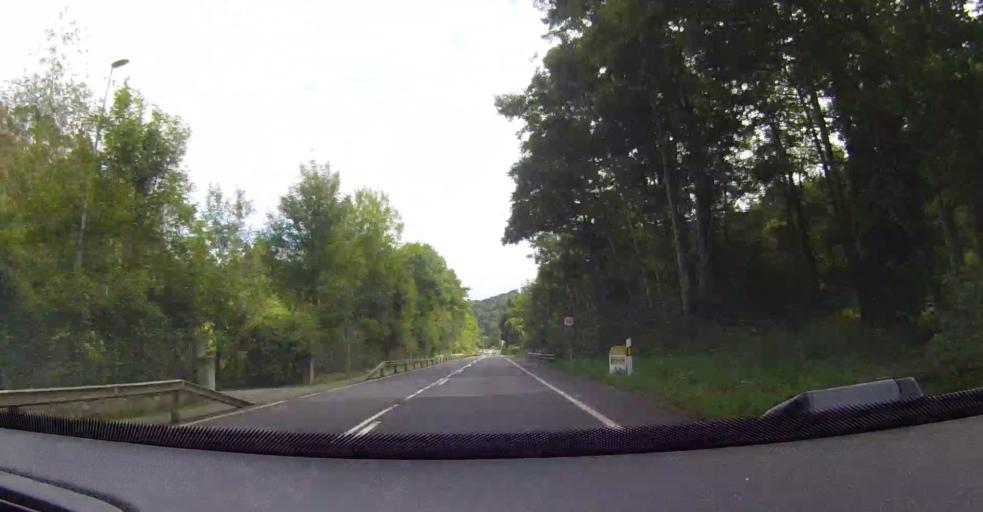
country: ES
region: Basque Country
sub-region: Bizkaia
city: Elantxobe
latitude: 43.3962
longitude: -2.6436
